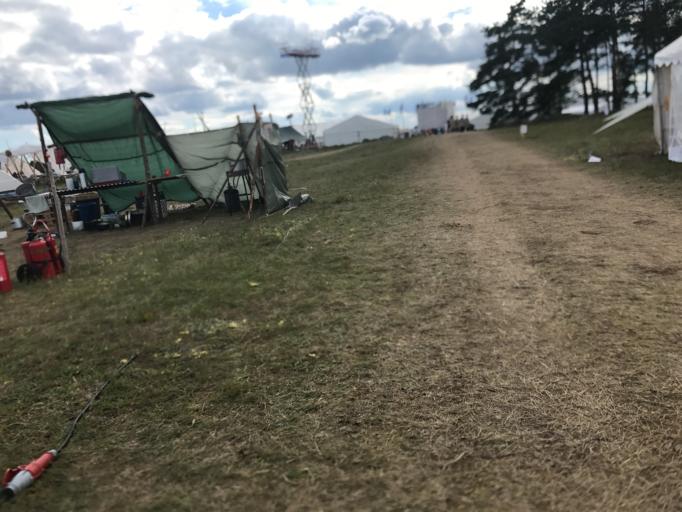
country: SE
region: Skane
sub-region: Kristianstads Kommun
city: Fjalkinge
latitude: 56.0075
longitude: 14.3031
